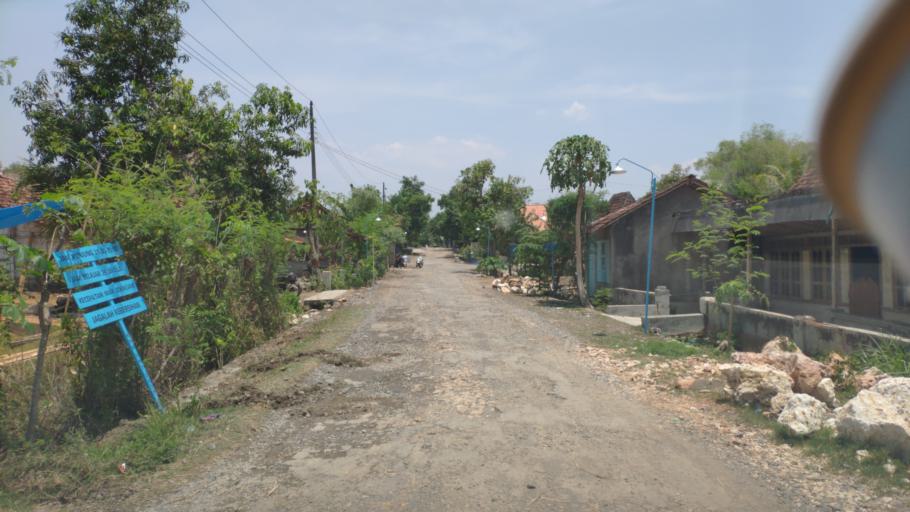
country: ID
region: Central Java
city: Karangtengah
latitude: -7.0421
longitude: 111.3118
